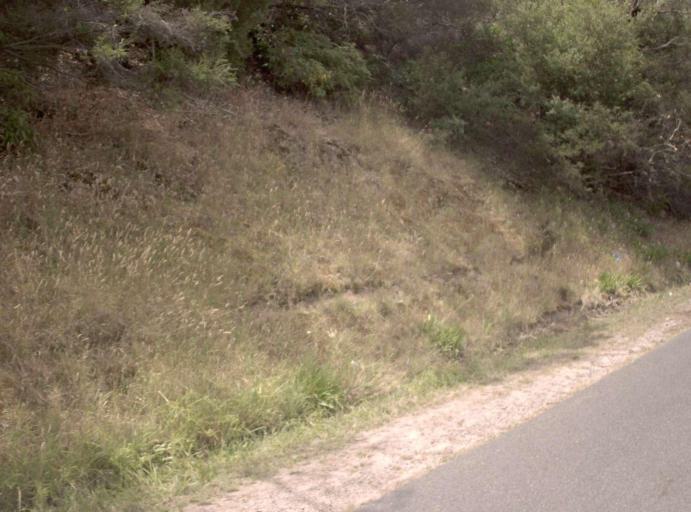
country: AU
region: Victoria
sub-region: Mornington Peninsula
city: McCrae
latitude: -38.3445
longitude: 144.9475
